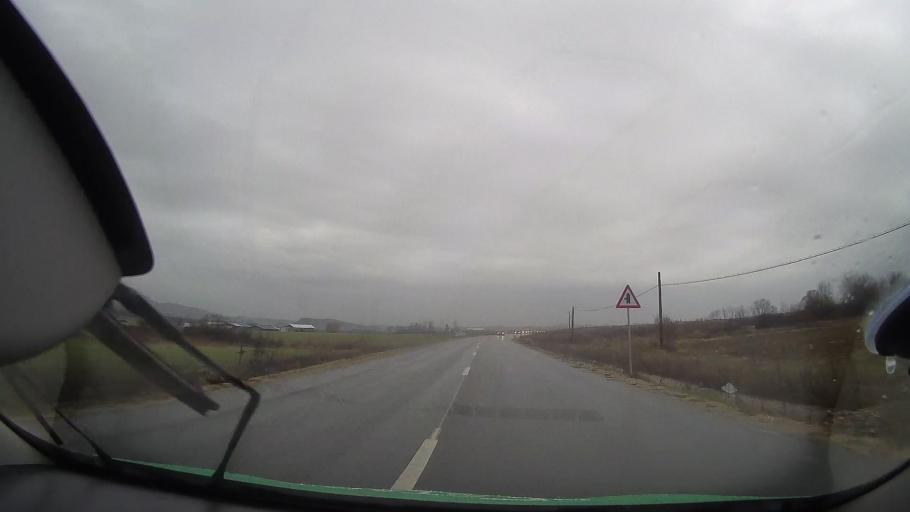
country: RO
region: Bihor
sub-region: Municipiul Beius
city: Beius
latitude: 46.6739
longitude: 22.3259
